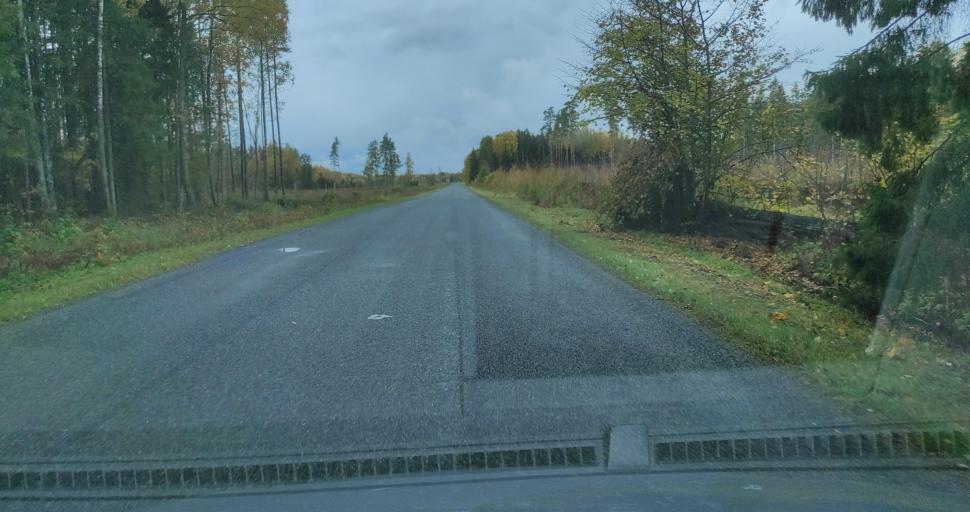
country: LV
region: Skrunda
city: Skrunda
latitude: 56.6067
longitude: 21.9242
